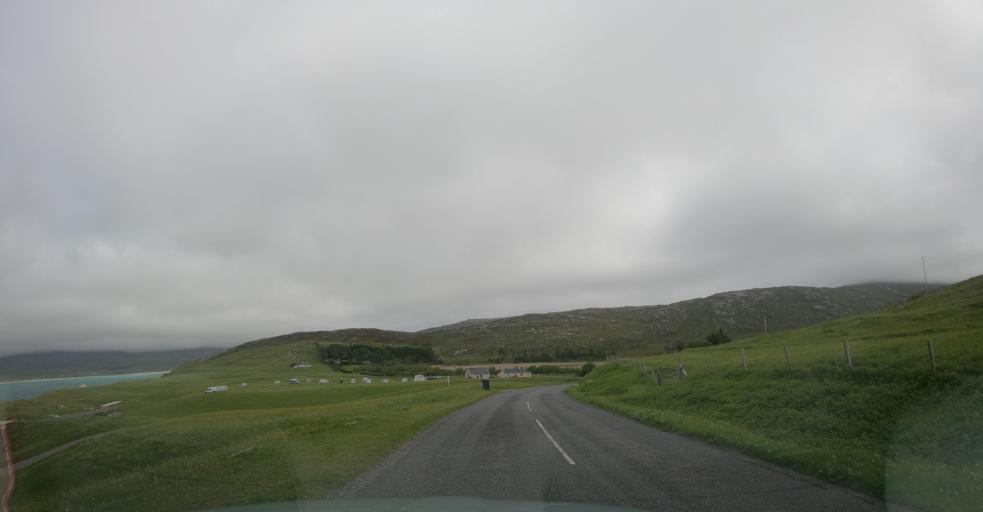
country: GB
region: Scotland
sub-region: Eilean Siar
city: Harris
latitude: 57.8615
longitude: -6.9827
